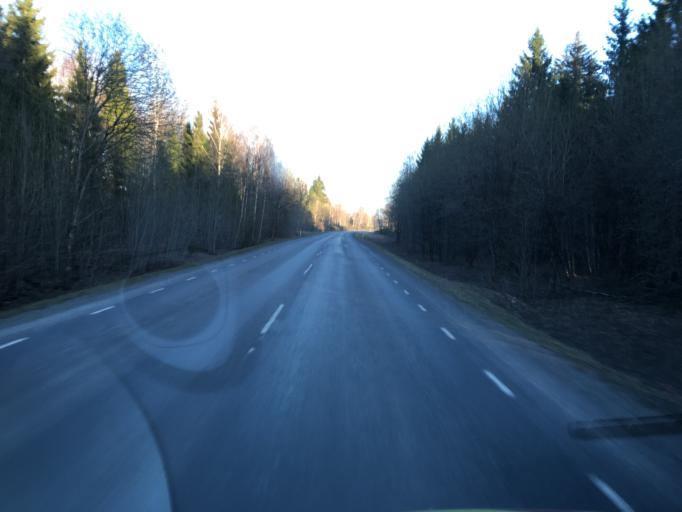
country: EE
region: Raplamaa
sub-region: Kehtna vald
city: Kehtna
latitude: 59.0637
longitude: 24.9306
